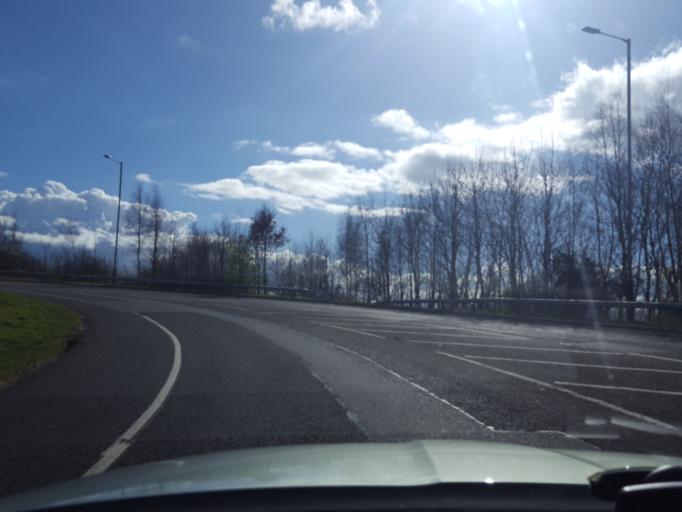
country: GB
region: Scotland
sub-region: Perth and Kinross
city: Errol
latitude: 56.4202
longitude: -3.2316
